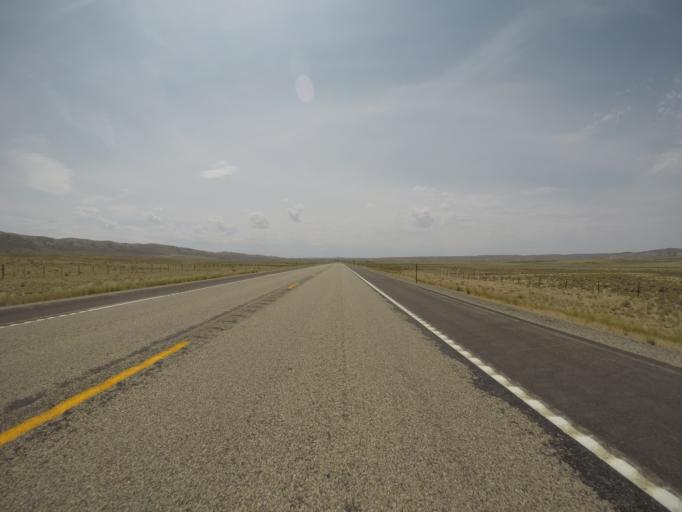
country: US
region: Wyoming
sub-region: Lincoln County
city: Kemmerer
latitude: 41.6519
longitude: -110.5710
